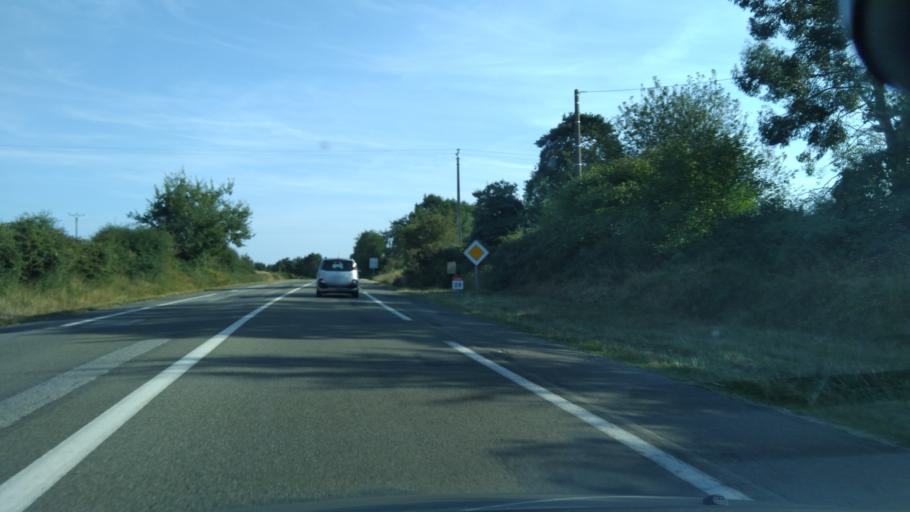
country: FR
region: Pays de la Loire
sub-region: Departement de la Mayenne
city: Entrammes
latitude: 47.9874
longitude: -0.7126
